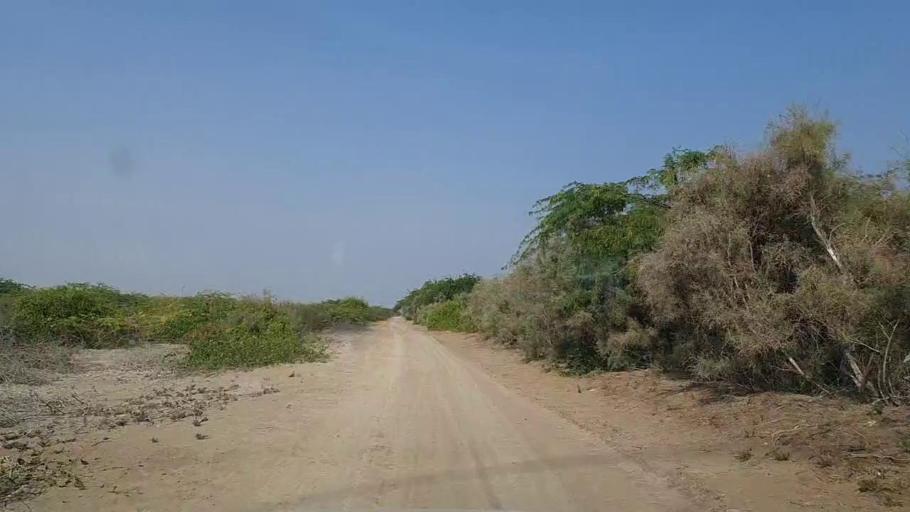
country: PK
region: Sindh
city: Mirpur Sakro
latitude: 24.5510
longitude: 67.5566
